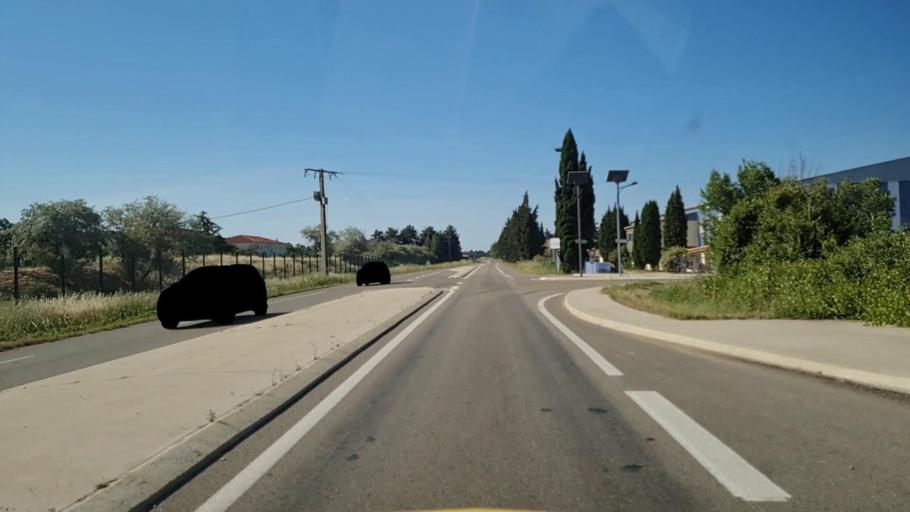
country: FR
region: Languedoc-Roussillon
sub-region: Departement du Gard
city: Garons
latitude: 43.7651
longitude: 4.4056
